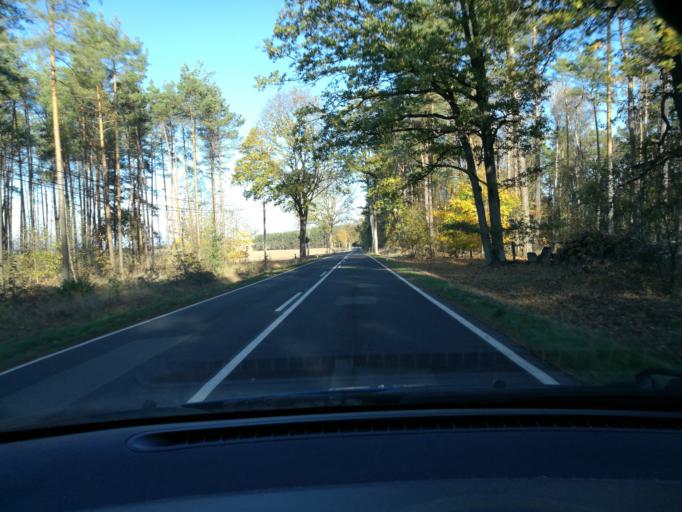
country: DE
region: Brandenburg
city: Lanz
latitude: 53.1375
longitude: 11.5622
